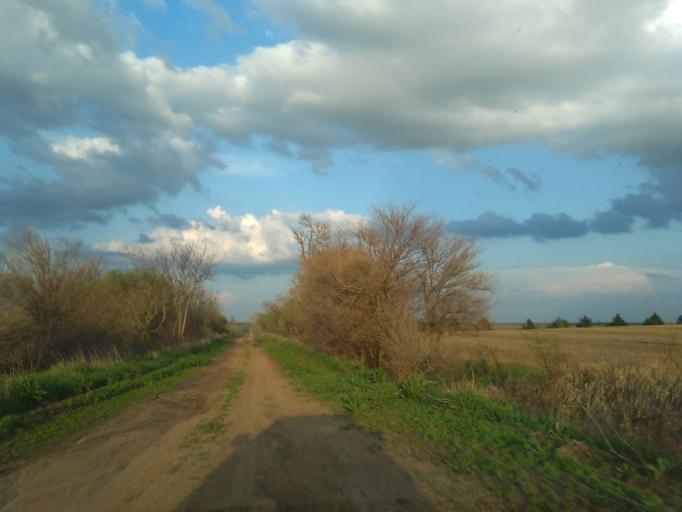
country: US
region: Nebraska
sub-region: Webster County
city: Red Cloud
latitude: 40.2054
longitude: -98.3783
